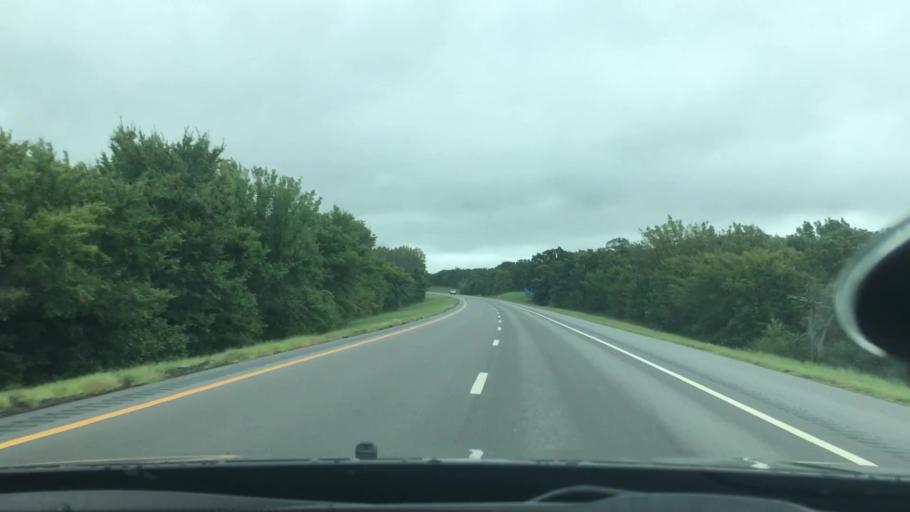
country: US
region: Oklahoma
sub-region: Okmulgee County
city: Henryetta
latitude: 35.4336
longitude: -95.7980
